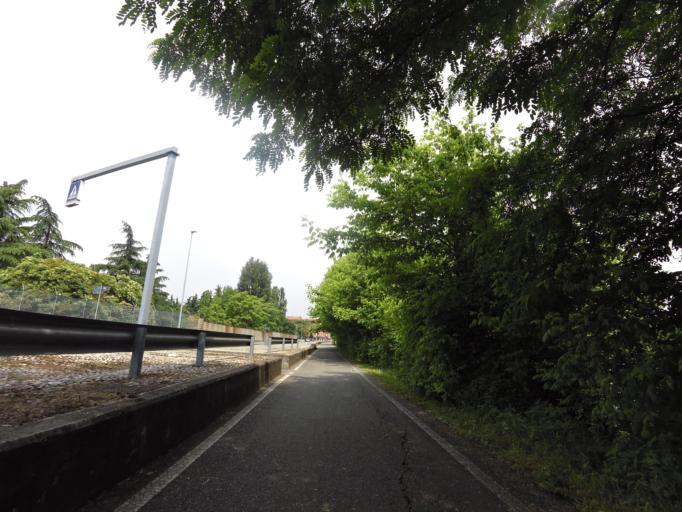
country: IT
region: Lombardy
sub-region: Citta metropolitana di Milano
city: Linate
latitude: 45.4428
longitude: 9.2730
